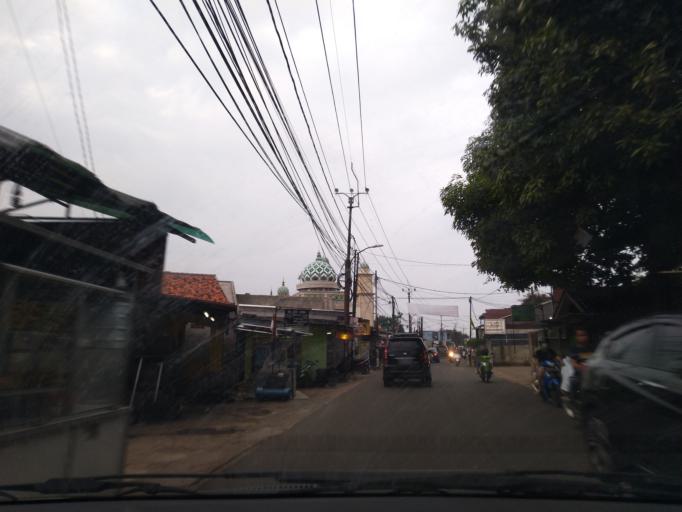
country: ID
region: Banten
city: South Tangerang
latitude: -6.2628
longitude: 106.7449
